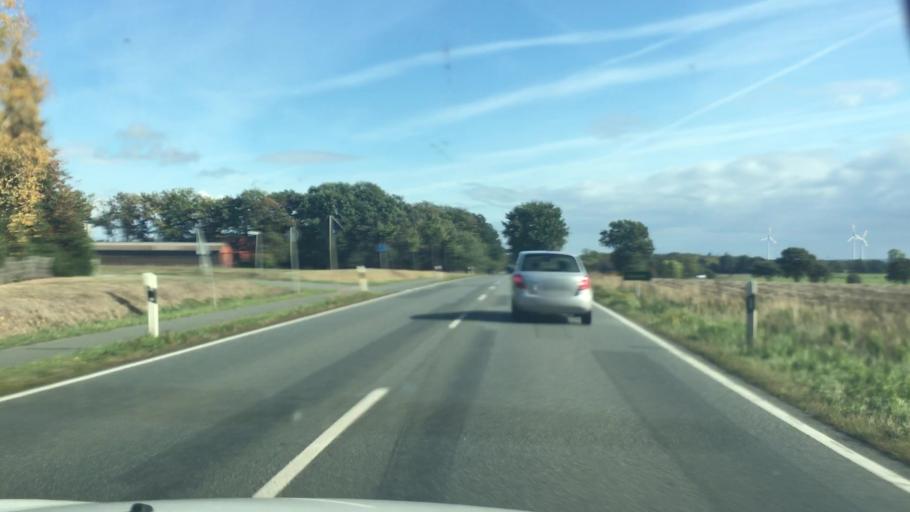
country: DE
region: Lower Saxony
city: Maasen
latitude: 52.6850
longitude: 8.8731
